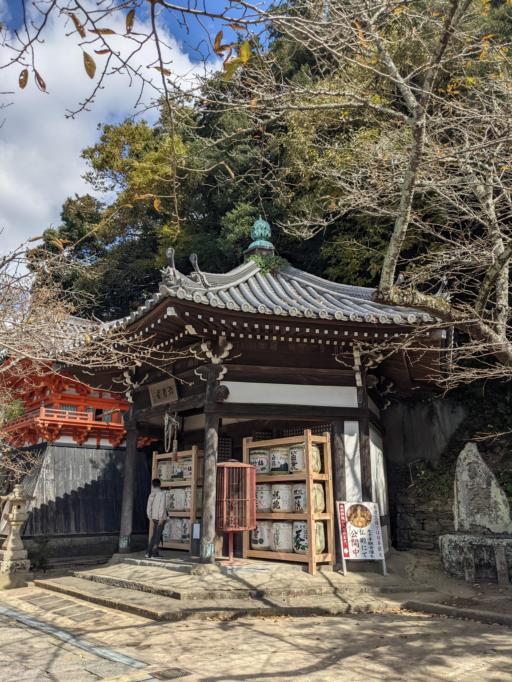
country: JP
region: Wakayama
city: Kainan
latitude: 34.1844
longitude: 135.1899
